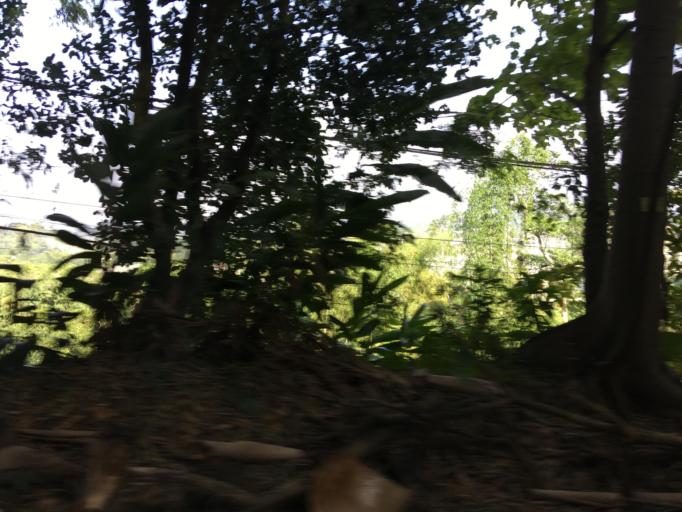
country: TW
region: Taiwan
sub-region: Chiayi
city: Jiayi Shi
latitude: 23.4946
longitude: 120.4854
